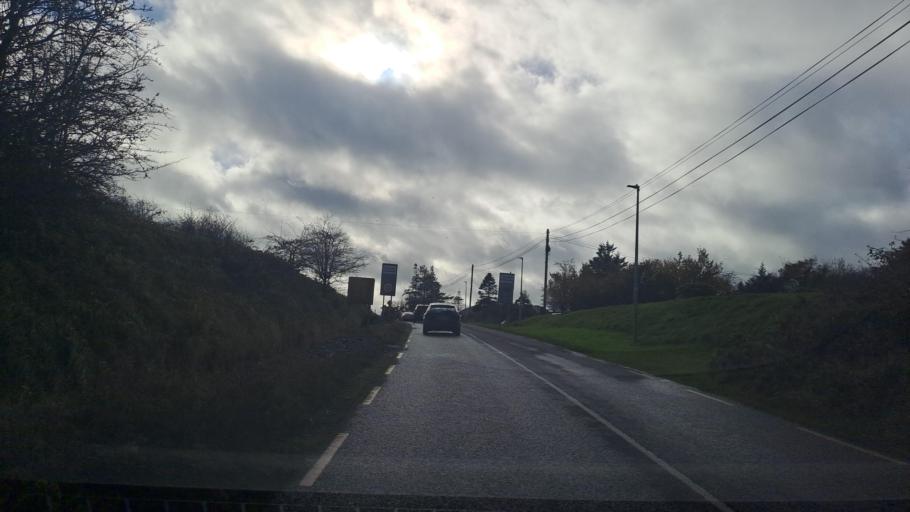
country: IE
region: Ulster
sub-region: County Monaghan
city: Monaghan
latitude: 54.1925
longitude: -6.9907
